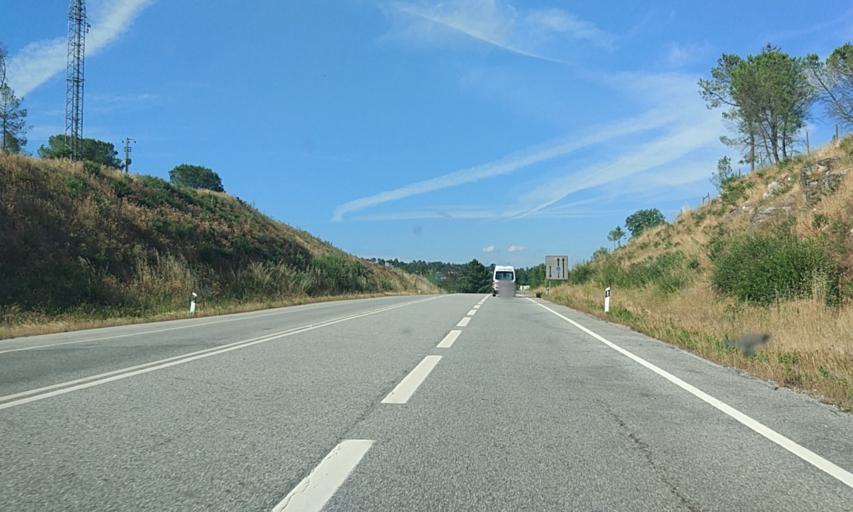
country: PT
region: Viseu
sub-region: Viseu
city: Viseu
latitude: 40.6087
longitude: -7.9624
